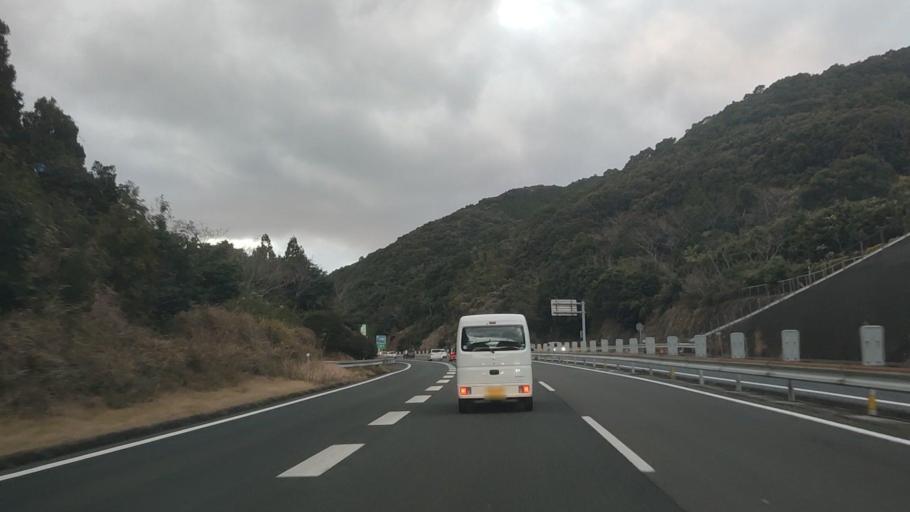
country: JP
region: Nagasaki
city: Obita
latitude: 32.8181
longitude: 129.9510
